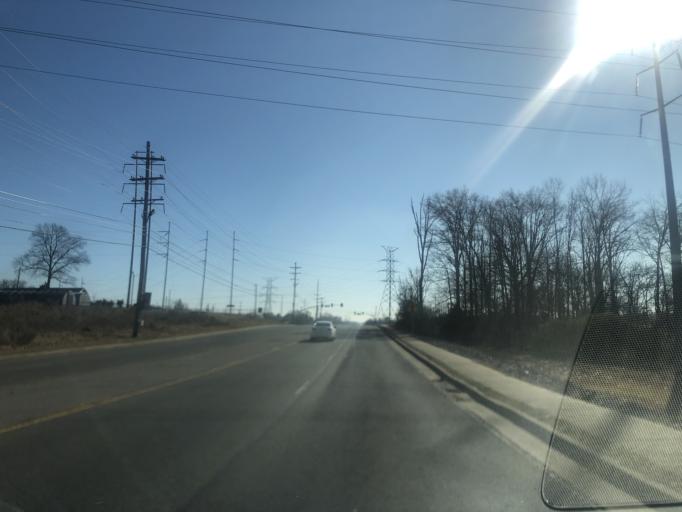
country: US
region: Tennessee
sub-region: Rutherford County
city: Smyrna
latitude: 35.9689
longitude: -86.5305
